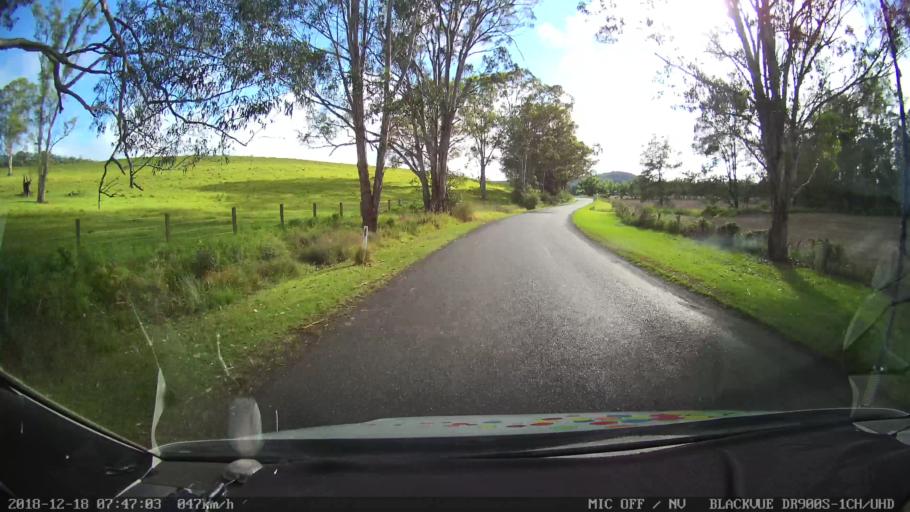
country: AU
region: New South Wales
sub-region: Kyogle
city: Kyogle
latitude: -28.4644
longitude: 152.5543
